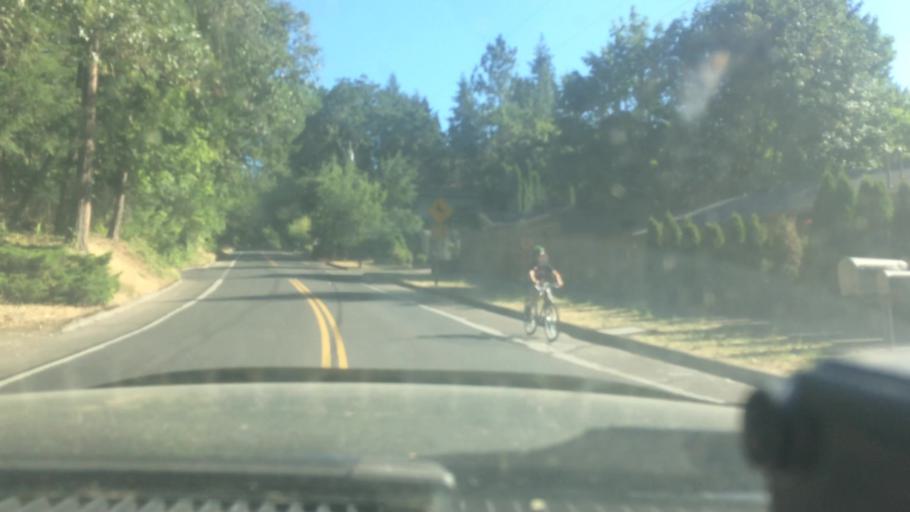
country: US
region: Oregon
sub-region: Lane County
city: Eugene
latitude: 44.0097
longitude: -123.0787
